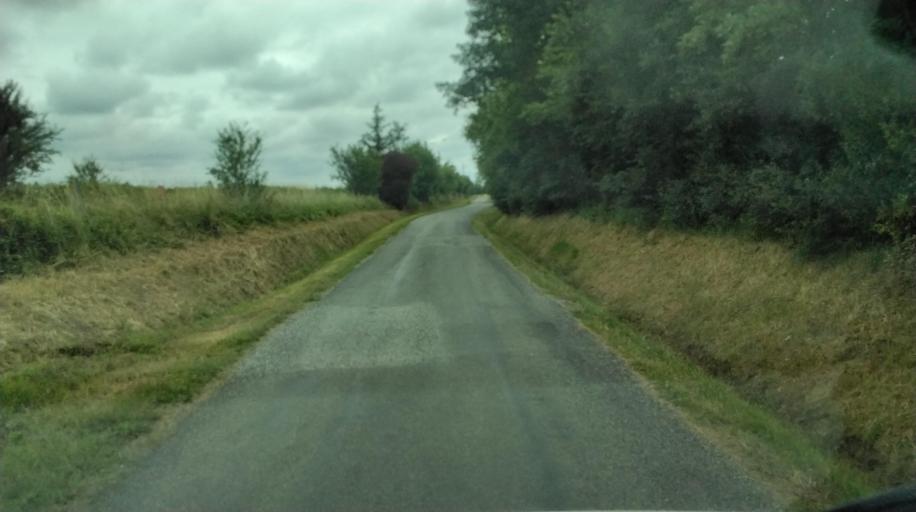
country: FR
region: Midi-Pyrenees
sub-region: Departement de la Haute-Garonne
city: Cazeres
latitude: 43.2126
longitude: 1.0517
